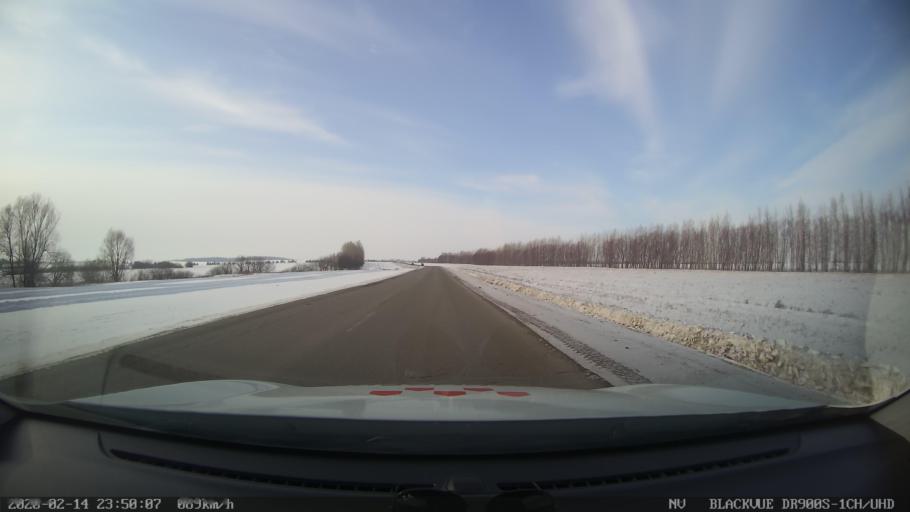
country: RU
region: Tatarstan
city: Kuybyshevskiy Zaton
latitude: 55.2577
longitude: 49.1673
